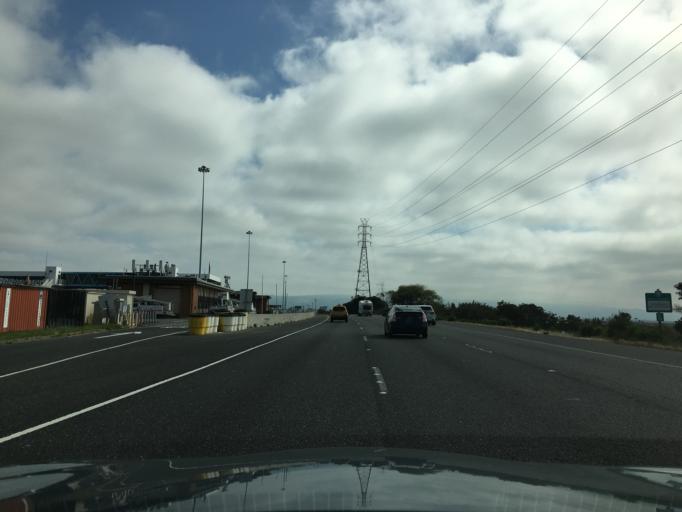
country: US
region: California
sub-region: Alameda County
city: San Lorenzo
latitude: 37.6171
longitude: -122.1541
